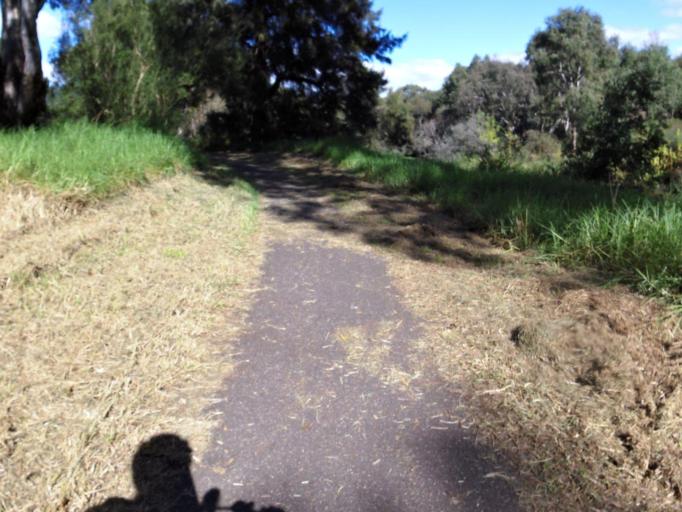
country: AU
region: Victoria
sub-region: Greater Geelong
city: Hamlyn Heights
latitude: -38.1454
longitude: 144.3136
